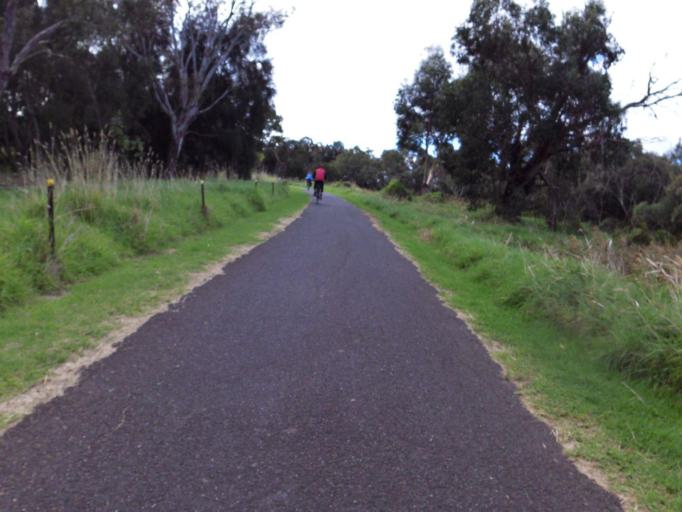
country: AU
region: Victoria
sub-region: Greater Geelong
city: Breakwater
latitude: -38.1767
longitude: 144.3608
